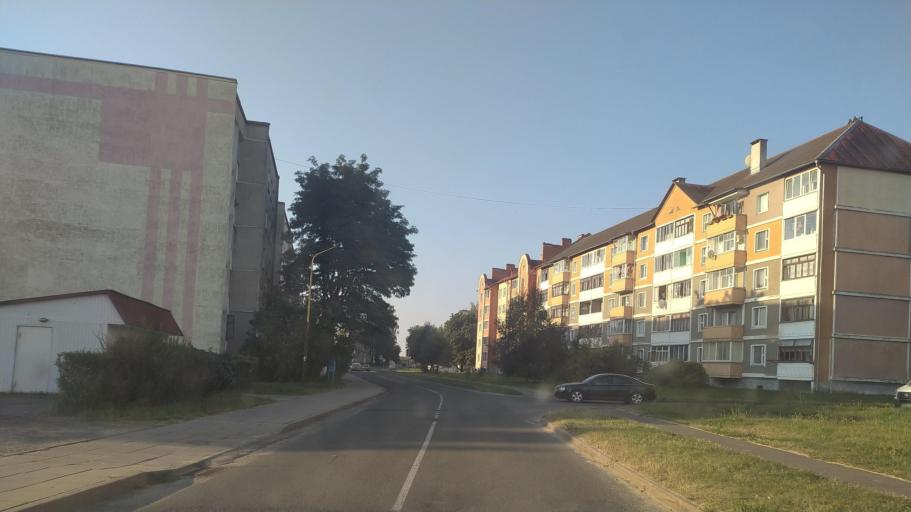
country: BY
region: Brest
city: Byaroza
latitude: 52.5441
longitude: 24.9844
